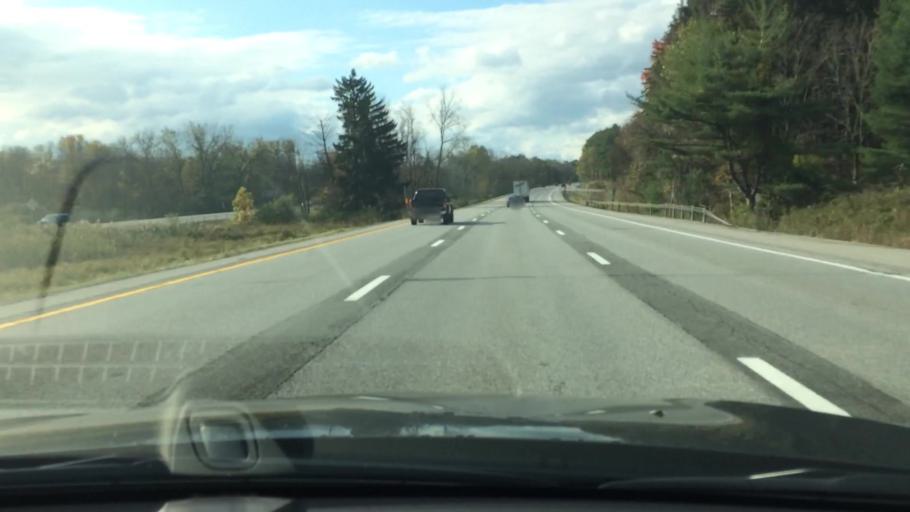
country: US
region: New York
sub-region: Saratoga County
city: Saratoga Springs
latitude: 43.0700
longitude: -73.7524
